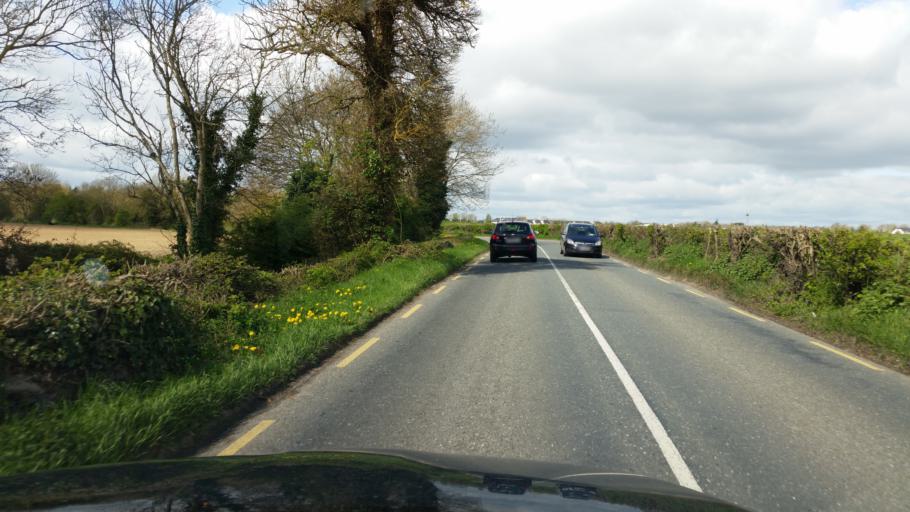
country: IE
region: Leinster
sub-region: An Mhi
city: Ashbourne
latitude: 53.4961
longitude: -6.3779
